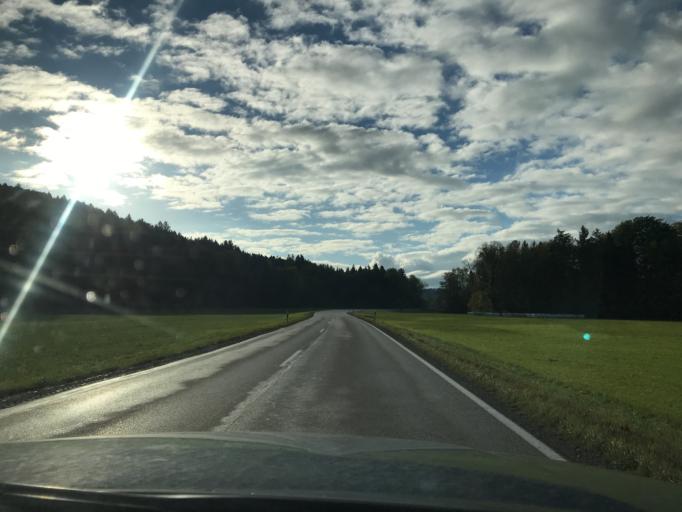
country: DE
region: Bavaria
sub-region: Upper Bavaria
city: Geretsried
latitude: 47.8450
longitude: 11.5241
